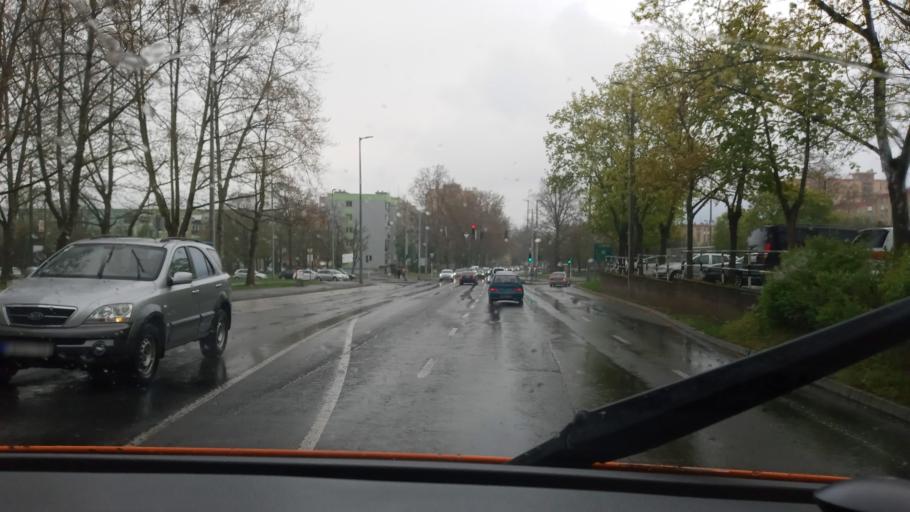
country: HU
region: Baranya
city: Pecs
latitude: 46.0415
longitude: 18.2164
